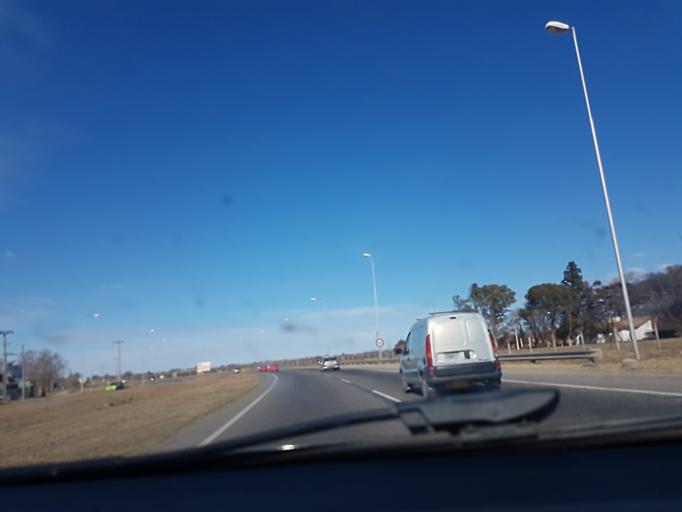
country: AR
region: Cordoba
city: La Calera
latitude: -31.4007
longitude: -64.2691
